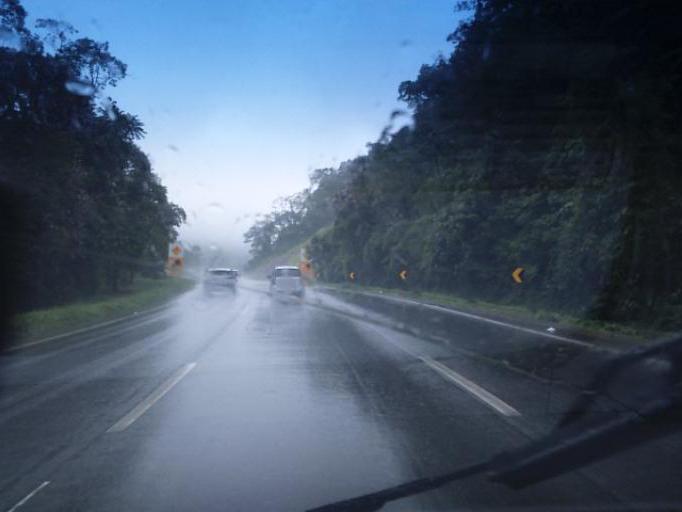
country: BR
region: Parana
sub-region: Guaratuba
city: Guaratuba
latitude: -25.8625
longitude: -48.9350
